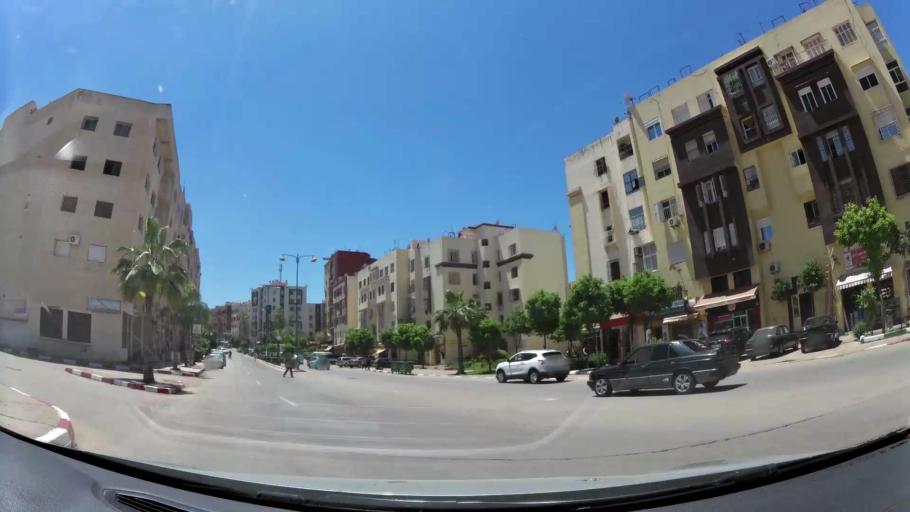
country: MA
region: Meknes-Tafilalet
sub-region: Meknes
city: Meknes
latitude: 33.8674
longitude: -5.5761
